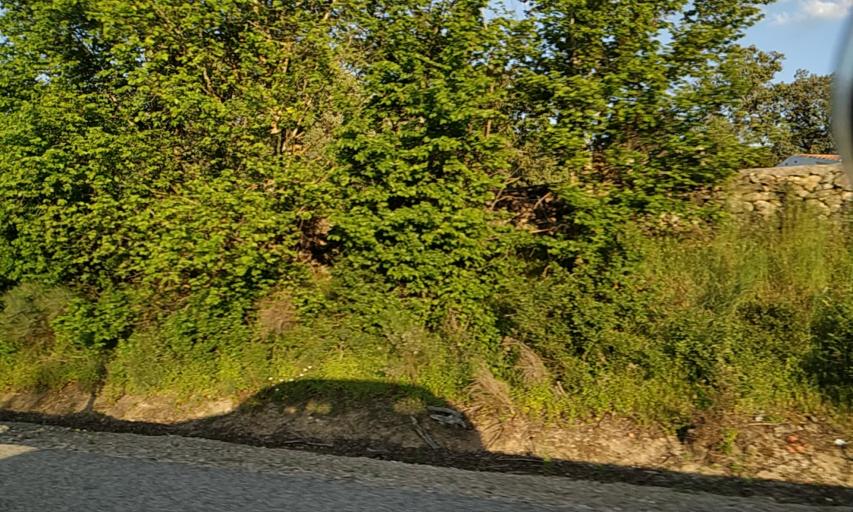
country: ES
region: Extremadura
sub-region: Provincia de Caceres
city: Valencia de Alcantara
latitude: 39.3778
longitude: -7.2529
